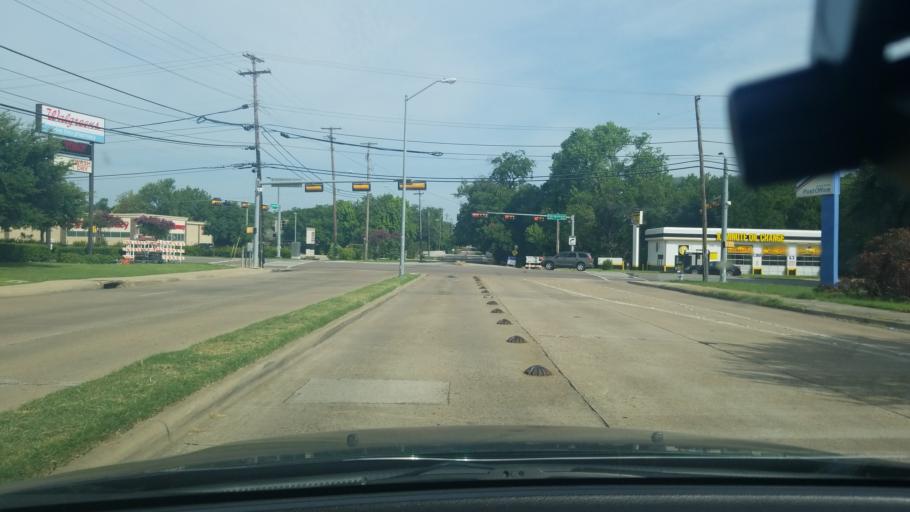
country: US
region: Texas
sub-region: Dallas County
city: Highland Park
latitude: 32.8115
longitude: -96.7008
